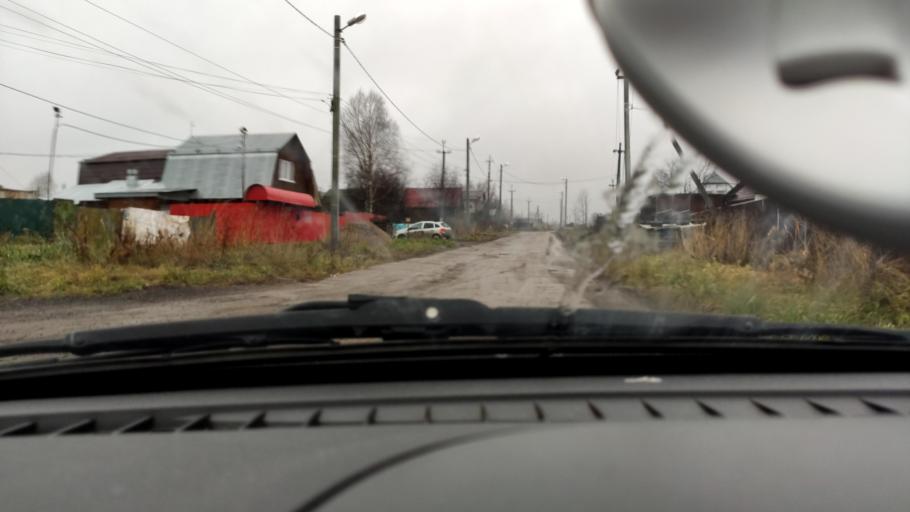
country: RU
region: Perm
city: Perm
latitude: 58.0361
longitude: 56.4090
